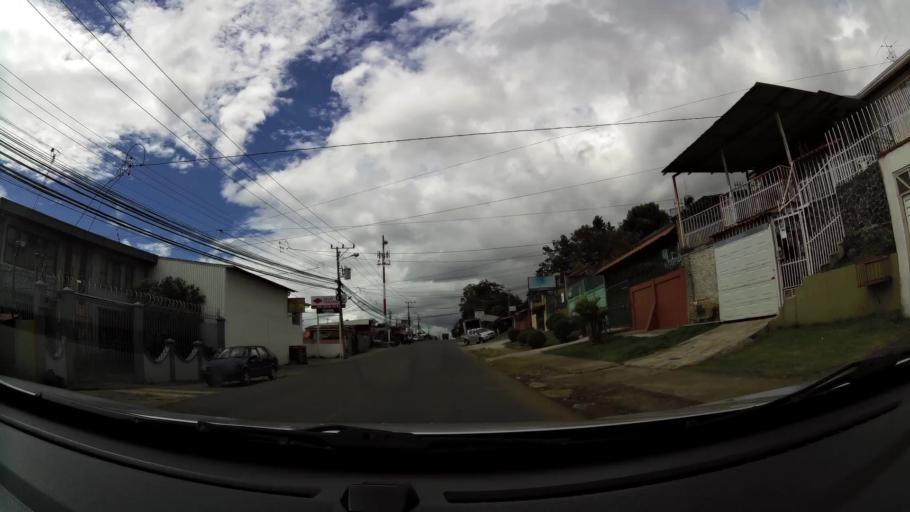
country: CR
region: Cartago
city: Tres Rios
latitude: 9.9090
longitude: -83.9915
